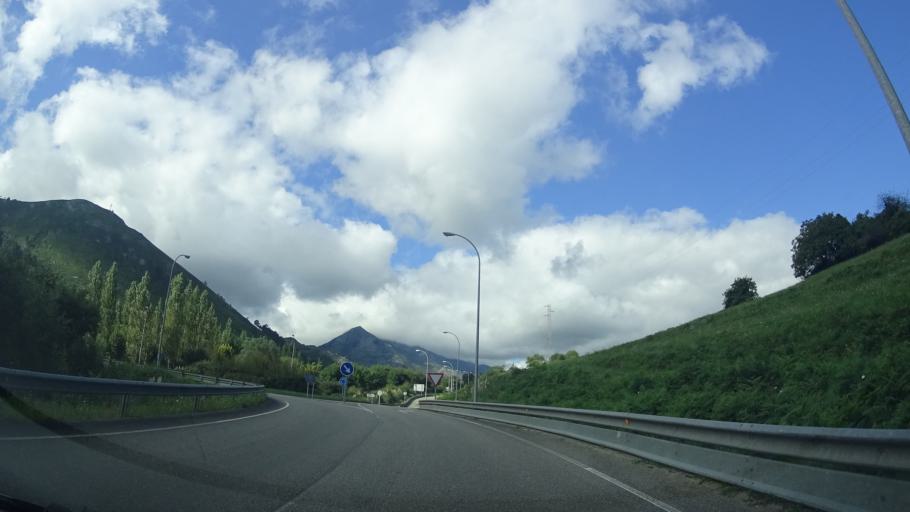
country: ES
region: Asturias
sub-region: Province of Asturias
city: Colunga
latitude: 43.4709
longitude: -5.1717
